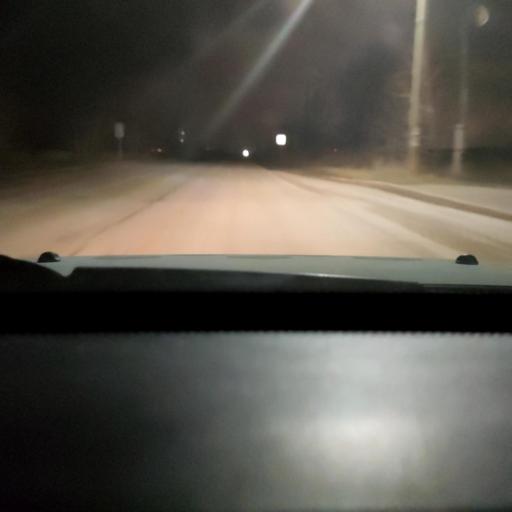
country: RU
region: Perm
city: Gamovo
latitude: 57.8751
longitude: 56.1019
